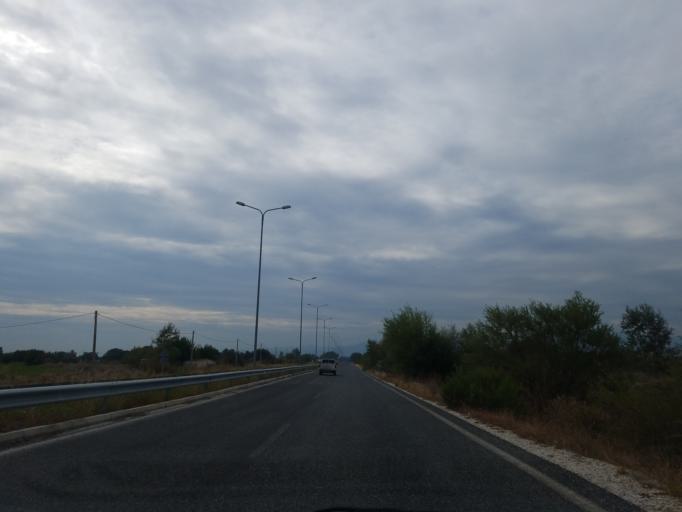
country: GR
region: Thessaly
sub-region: Trikala
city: Pyrgetos
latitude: 39.5560
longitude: 21.7337
